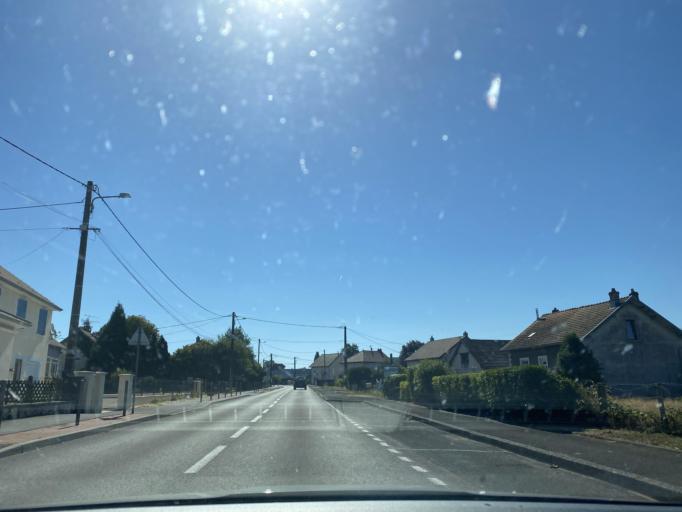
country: FR
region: Franche-Comte
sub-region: Departement de la Haute-Saone
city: Champagney
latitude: 47.7037
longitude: 6.6913
